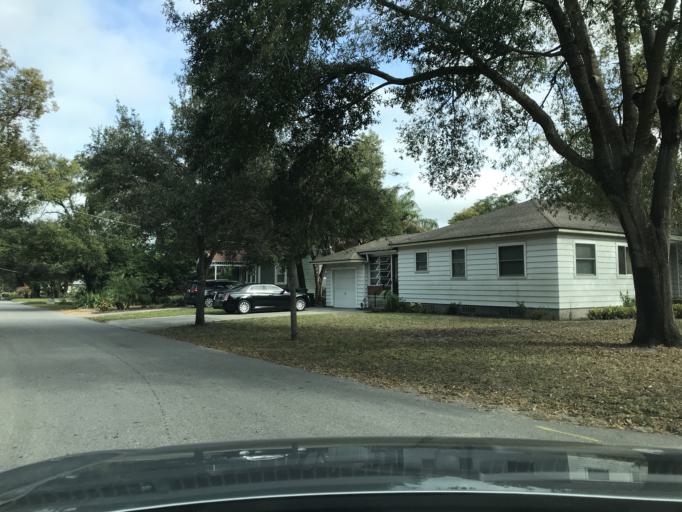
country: US
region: Florida
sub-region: Hillsborough County
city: Egypt Lake-Leto
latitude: 27.9997
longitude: -82.4610
